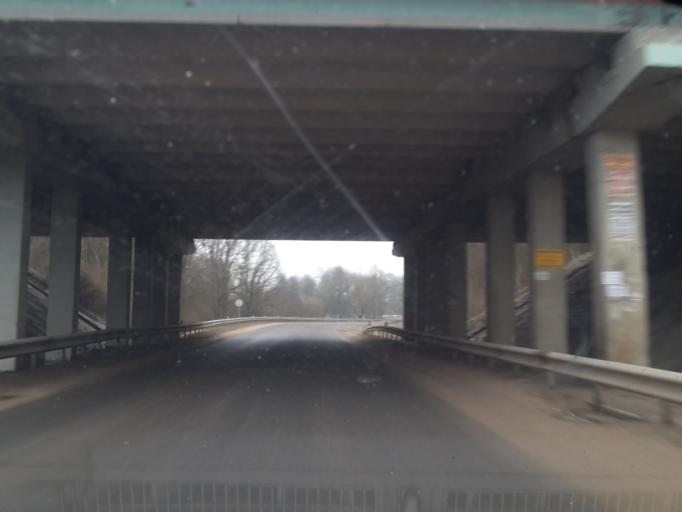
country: BY
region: Minsk
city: Zhdanovichy
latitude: 53.9103
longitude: 27.3912
